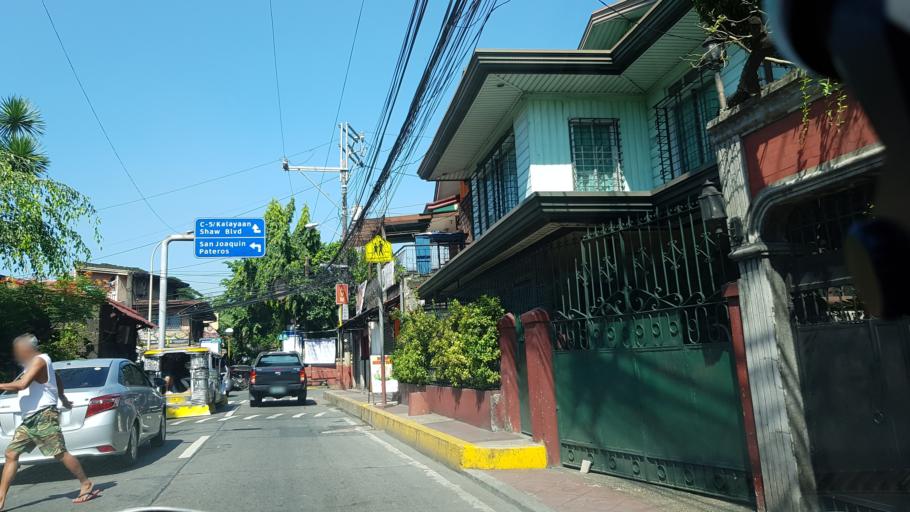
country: PH
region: Calabarzon
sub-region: Province of Rizal
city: Pateros
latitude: 14.5596
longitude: 121.0740
